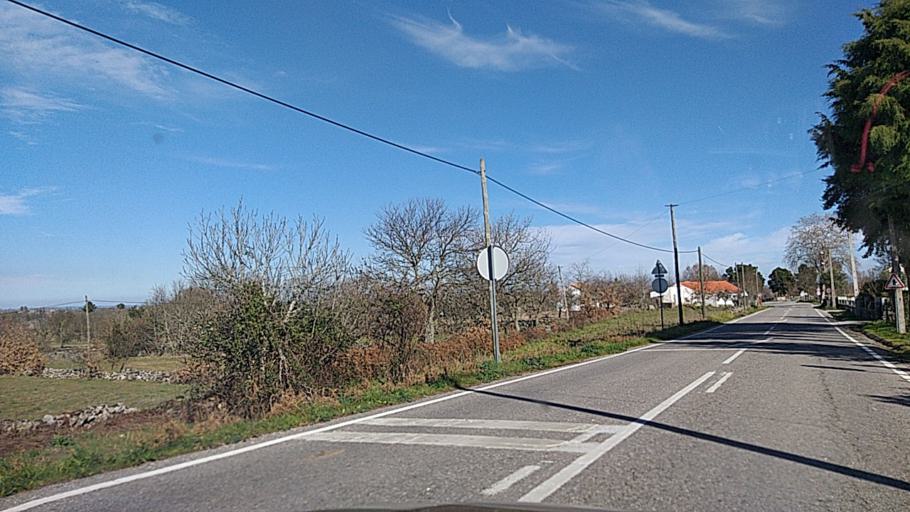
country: PT
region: Guarda
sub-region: Guarda
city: Sequeira
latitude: 40.5958
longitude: -7.1257
